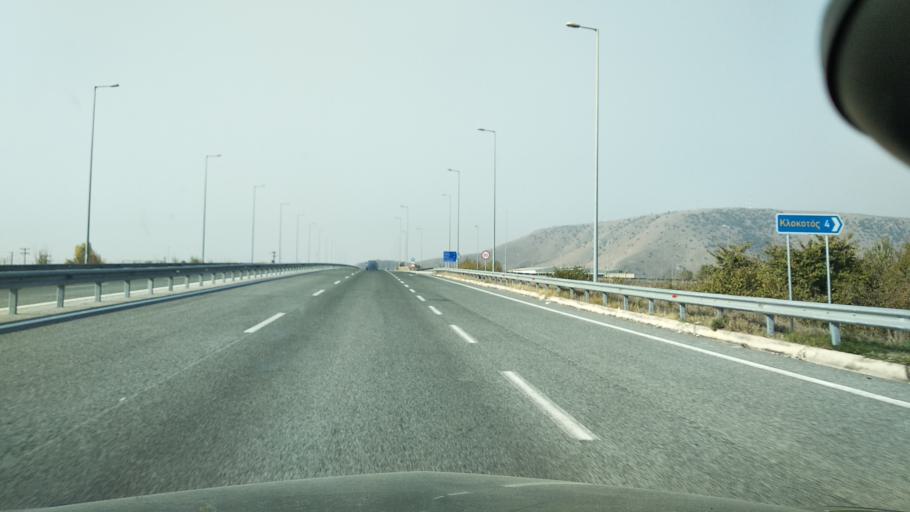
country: GR
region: Thessaly
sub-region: Trikala
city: Oichalia
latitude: 39.5715
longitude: 21.9888
